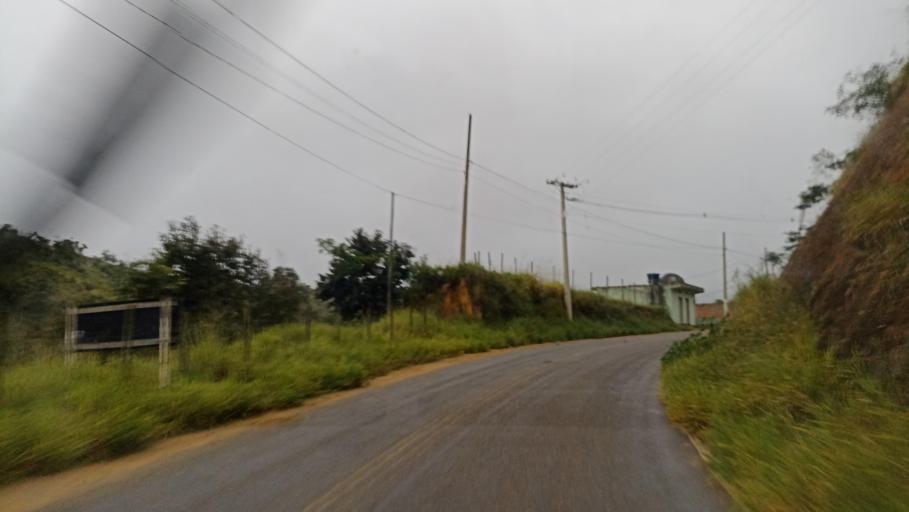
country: BR
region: Bahia
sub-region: Itanhem
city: Itanhem
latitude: -16.7348
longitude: -40.4295
